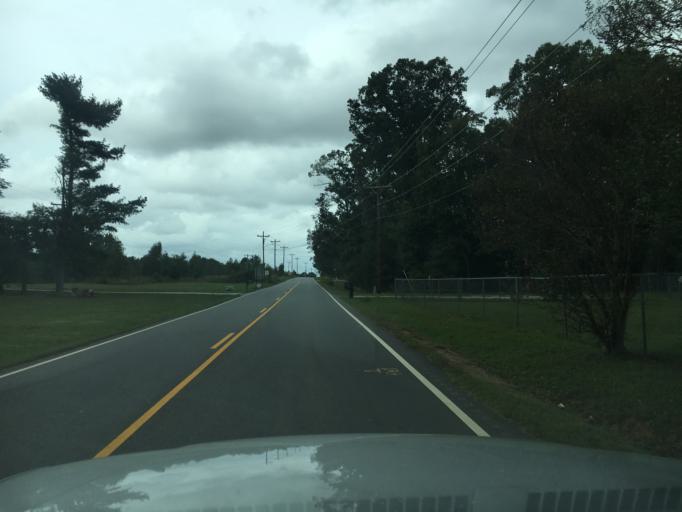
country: US
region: South Carolina
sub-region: Spartanburg County
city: Duncan
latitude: 34.8715
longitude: -82.1191
